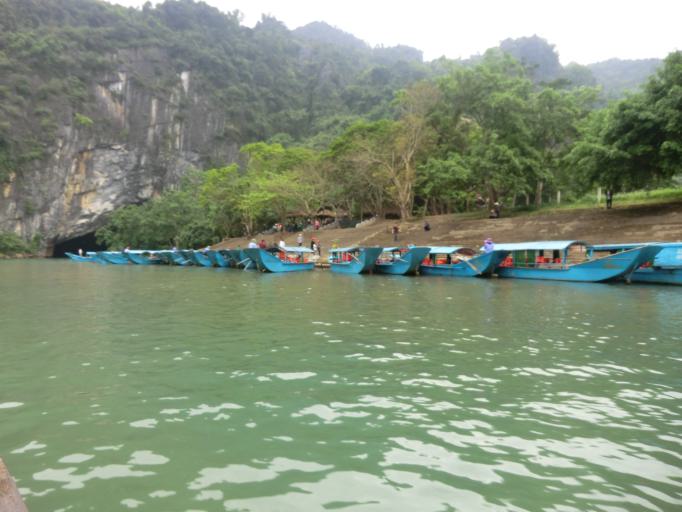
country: VN
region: Quang Binh
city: Ba Don
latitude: 17.5831
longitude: 106.2819
